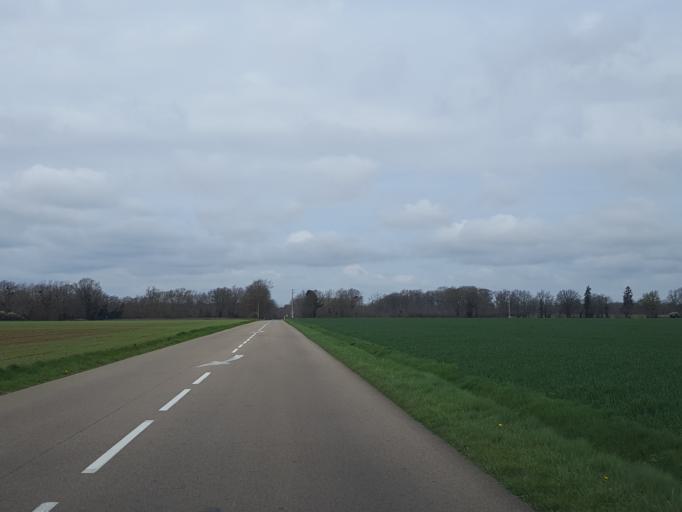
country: FR
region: Centre
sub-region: Departement du Loiret
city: Sainte-Genevieve-des-Bois
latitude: 47.8209
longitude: 2.8283
